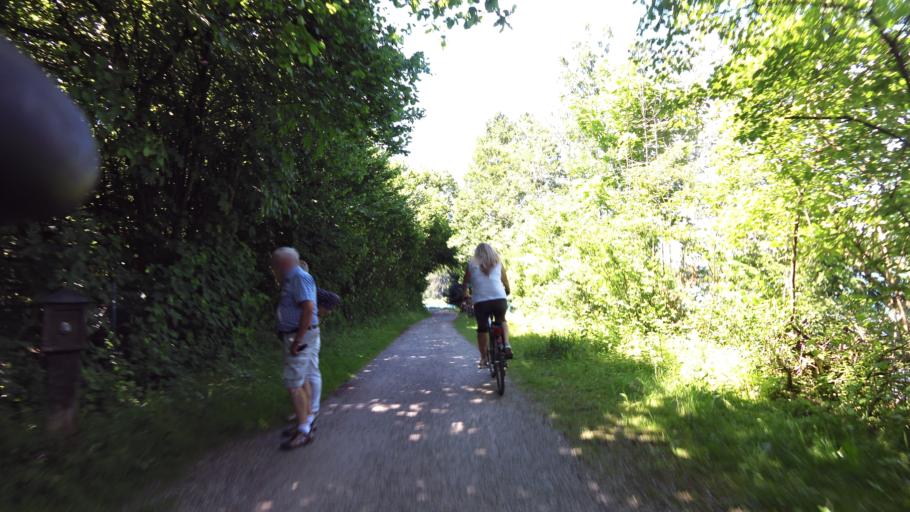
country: DE
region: Bavaria
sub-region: Upper Bavaria
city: Bad Wiessee
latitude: 47.7227
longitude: 11.7242
